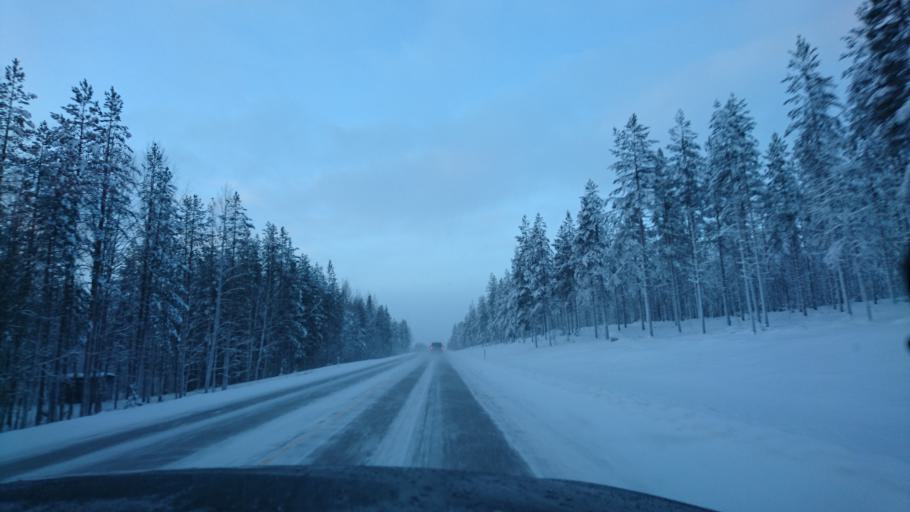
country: FI
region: Northern Ostrobothnia
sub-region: Koillismaa
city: Taivalkoski
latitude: 65.4882
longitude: 27.8698
